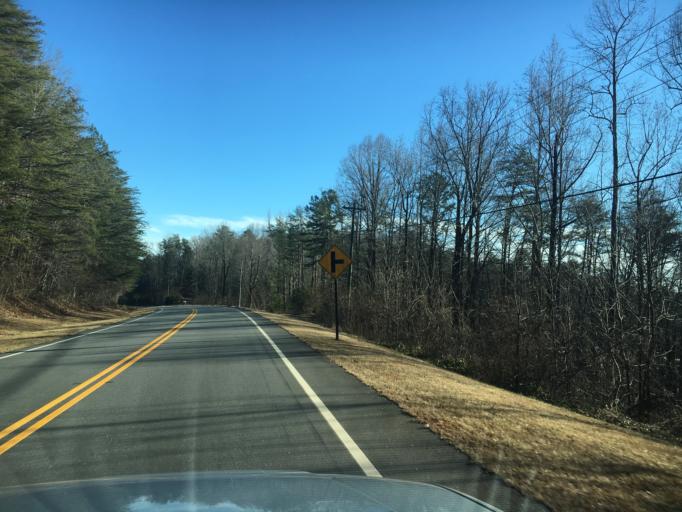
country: US
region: Georgia
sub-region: White County
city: Cleveland
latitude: 34.6627
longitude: -83.8549
